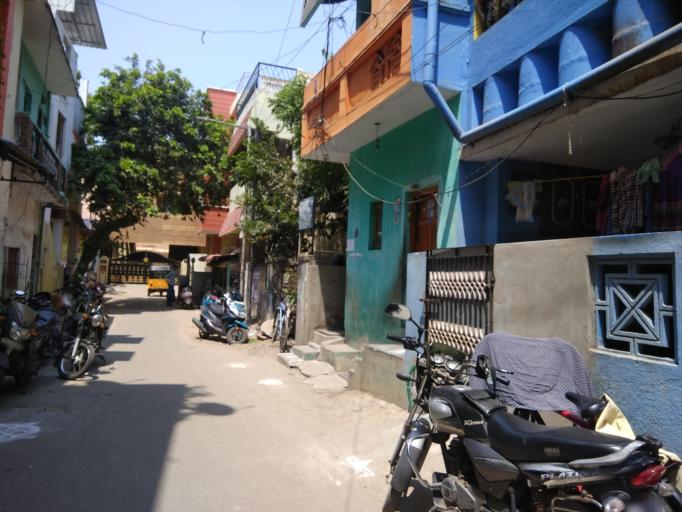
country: IN
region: Tamil Nadu
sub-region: Kancheepuram
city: Alandur
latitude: 13.0307
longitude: 80.2218
